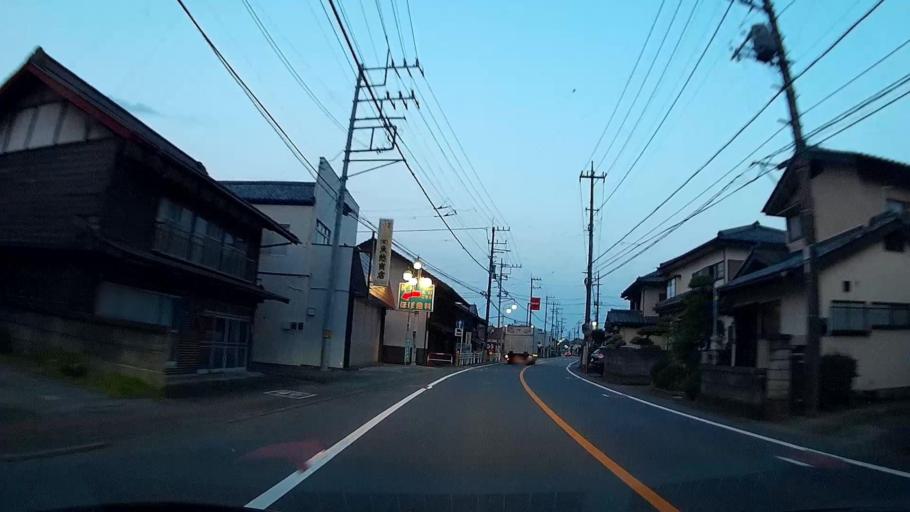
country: JP
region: Gunma
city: Annaka
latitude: 36.3791
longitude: 138.8863
